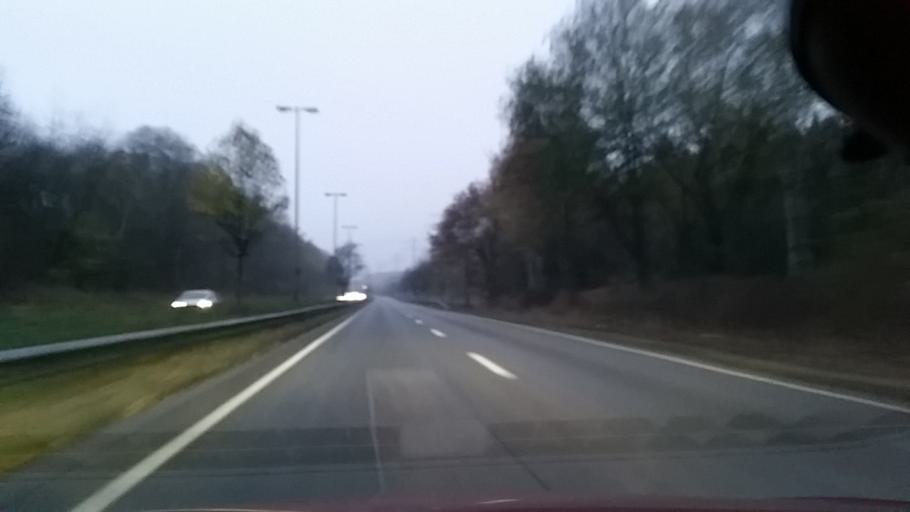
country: DE
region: Schleswig-Holstein
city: Wedel
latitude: 53.5807
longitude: 9.7742
